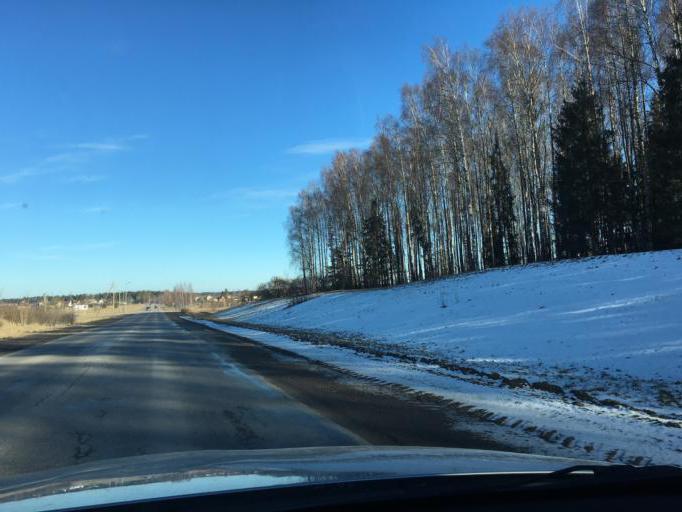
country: LV
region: Jekabpils Rajons
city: Jekabpils
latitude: 56.4865
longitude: 25.8641
